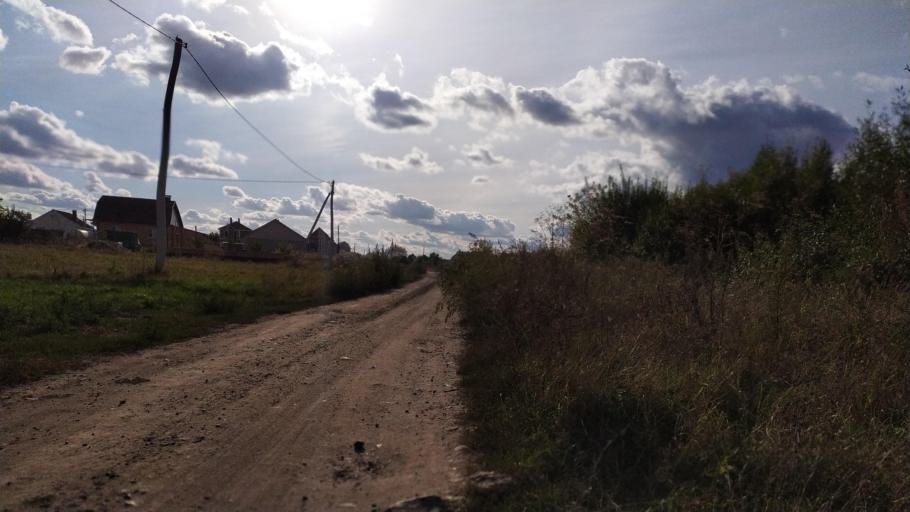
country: RU
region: Kursk
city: Kursk
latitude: 51.6409
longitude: 36.1577
